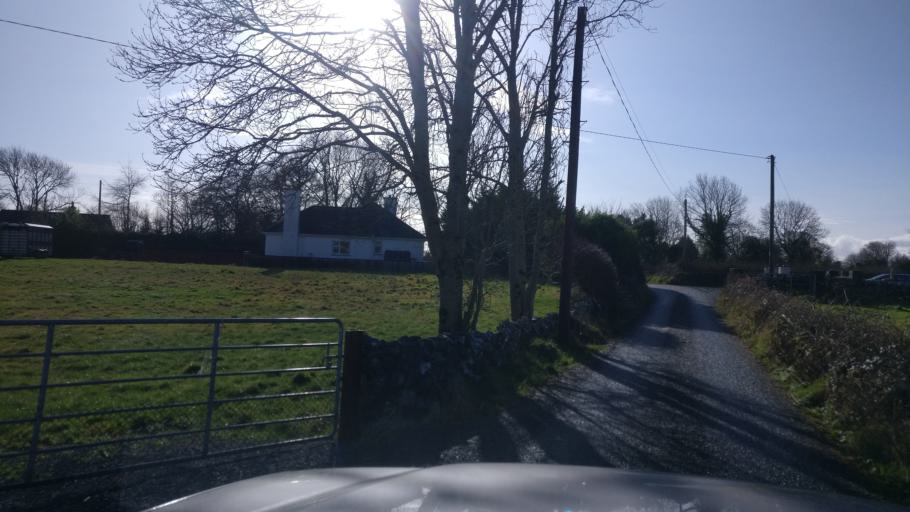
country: IE
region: Connaught
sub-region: County Galway
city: Athenry
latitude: 53.2356
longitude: -8.7791
